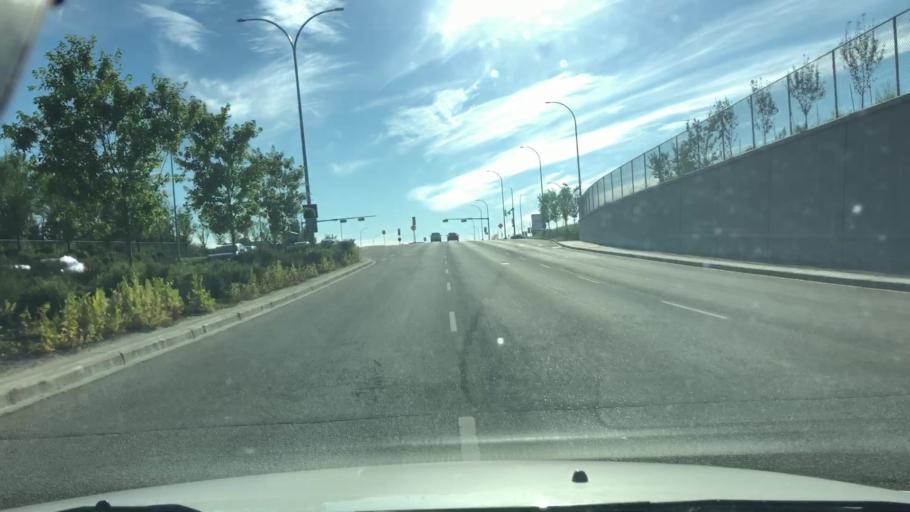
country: CA
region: Alberta
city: St. Albert
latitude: 53.5995
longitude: -113.5659
